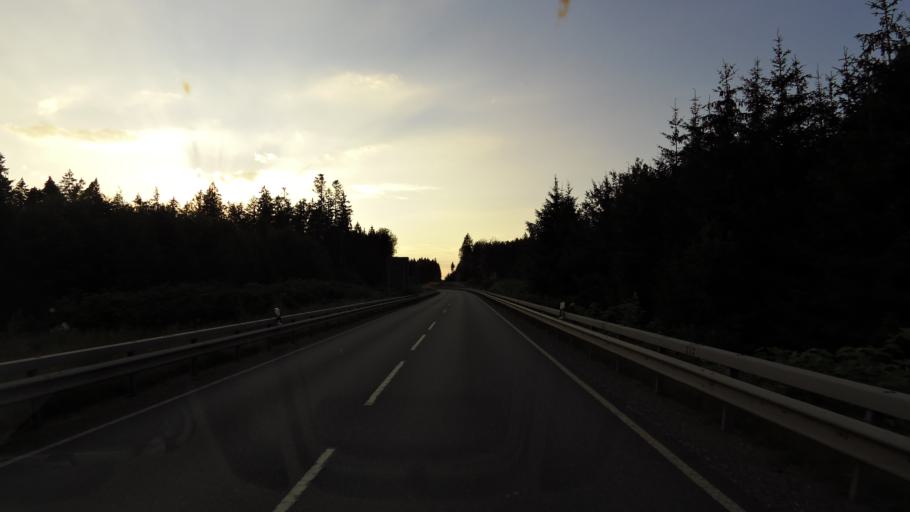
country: DE
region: Bavaria
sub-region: Upper Bavaria
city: Traunstein
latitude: 47.8895
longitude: 12.6448
